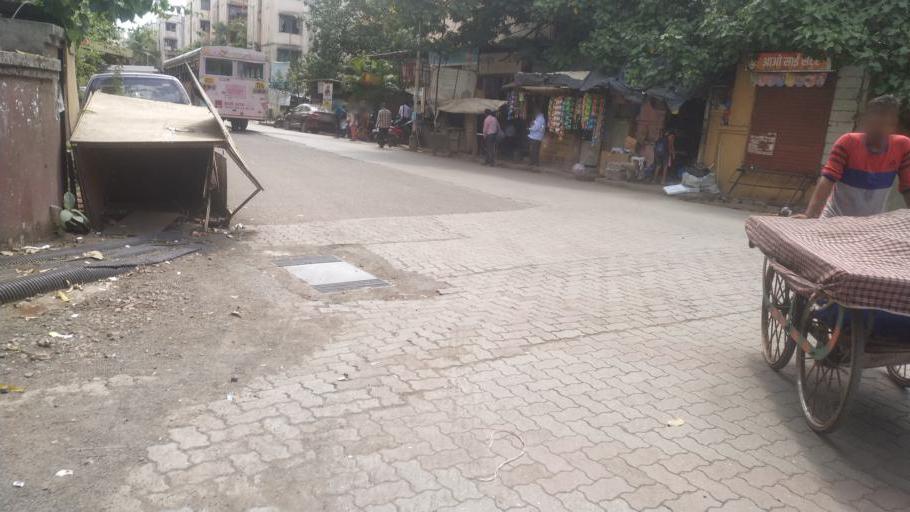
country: IN
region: Maharashtra
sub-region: Mumbai Suburban
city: Mumbai
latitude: 19.0448
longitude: 72.8749
